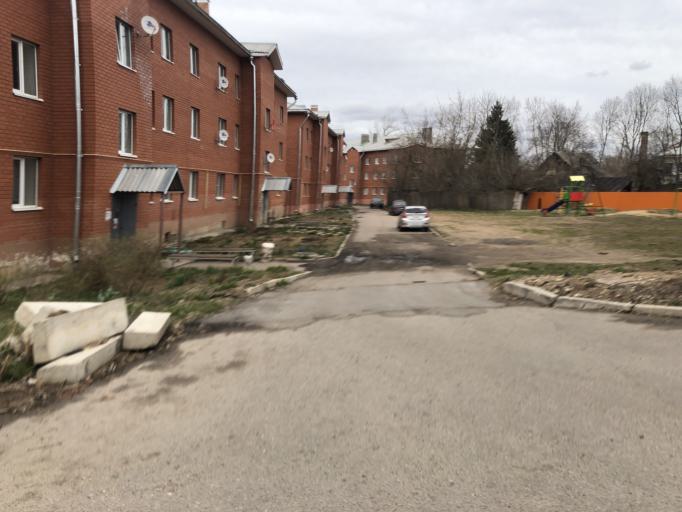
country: RU
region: Tverskaya
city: Rzhev
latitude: 56.2571
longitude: 34.3195
